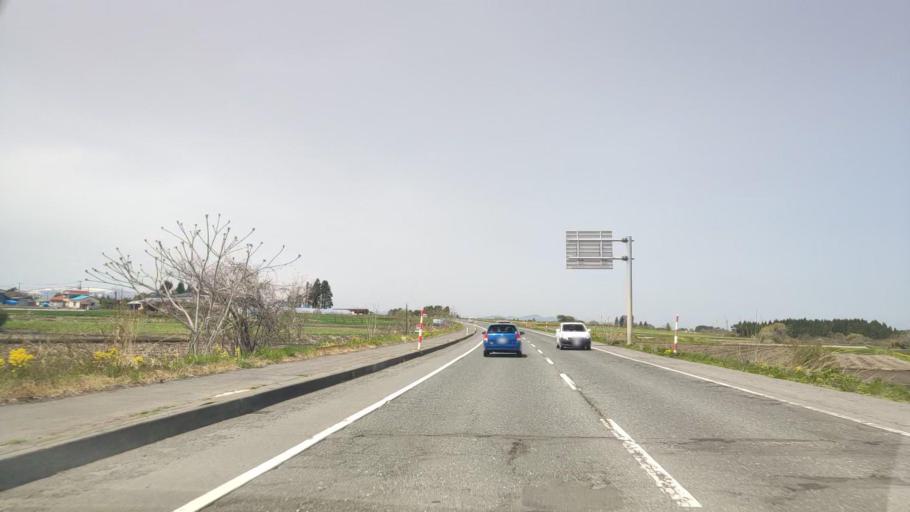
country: JP
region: Aomori
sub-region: Misawa Shi
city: Inuotose
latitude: 40.6351
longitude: 141.2440
